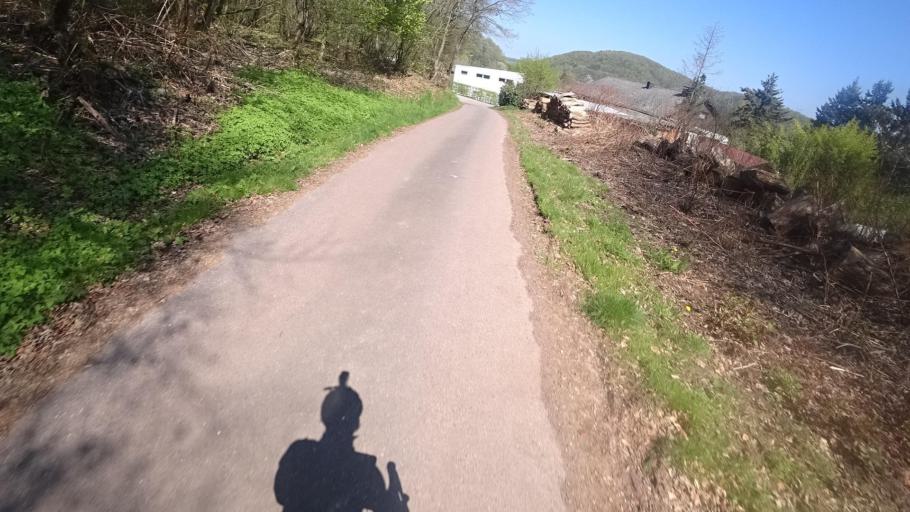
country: DE
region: Rheinland-Pfalz
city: Tawern
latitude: 49.6672
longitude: 6.5127
